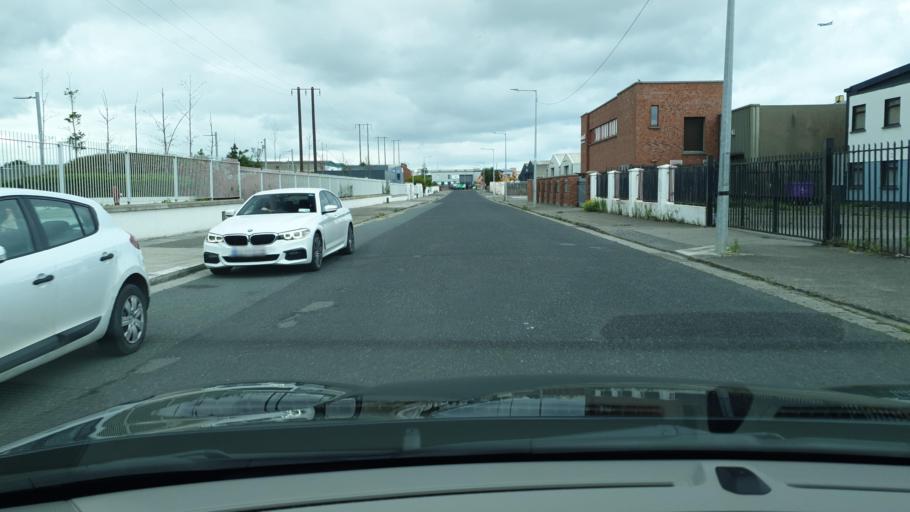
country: IE
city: Bayside
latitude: 53.3955
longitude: -6.1499
